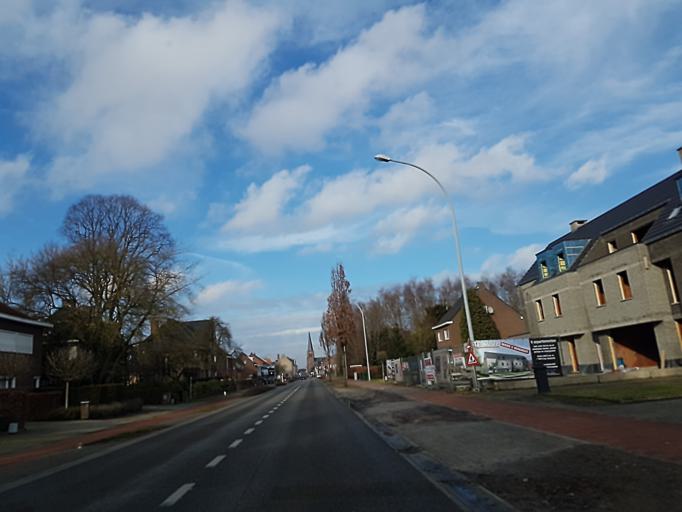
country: BE
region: Flanders
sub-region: Provincie Antwerpen
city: Dessel
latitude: 51.2345
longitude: 5.1137
